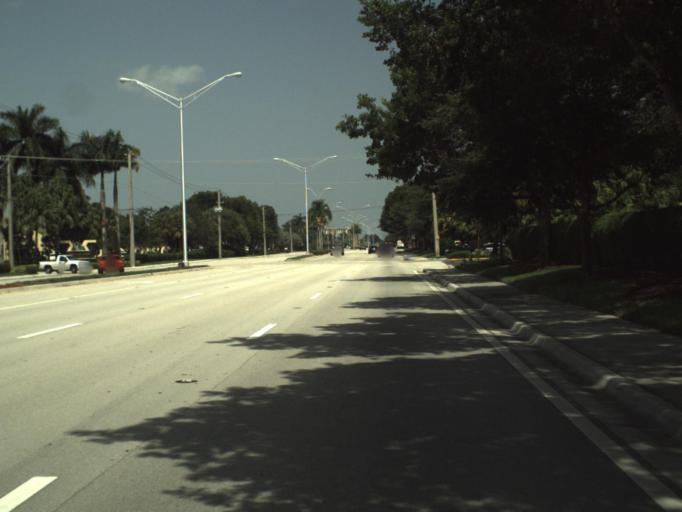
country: US
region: Florida
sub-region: Broward County
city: Coral Springs
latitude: 26.2728
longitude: -80.2874
